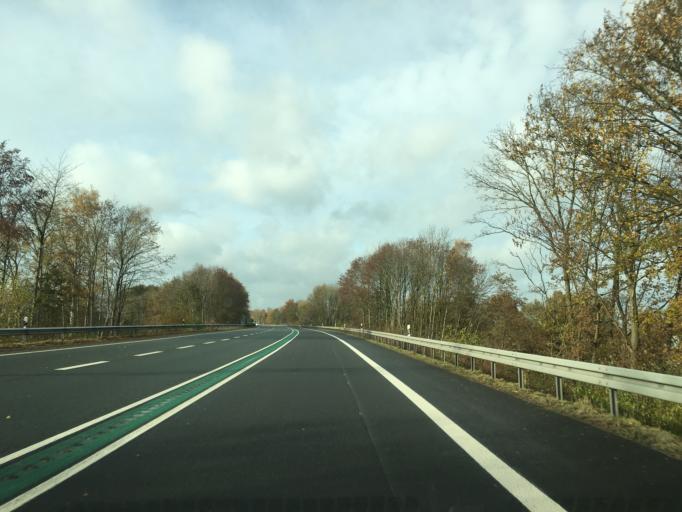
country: DE
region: North Rhine-Westphalia
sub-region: Regierungsbezirk Munster
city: Steinfurt
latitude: 52.1595
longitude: 7.3381
